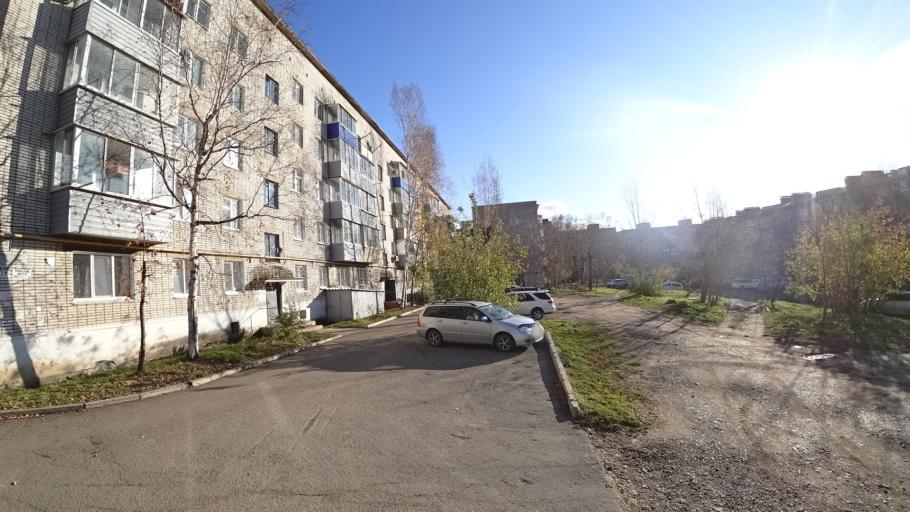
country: RU
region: Khabarovsk Krai
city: Amursk
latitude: 50.2296
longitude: 136.9109
